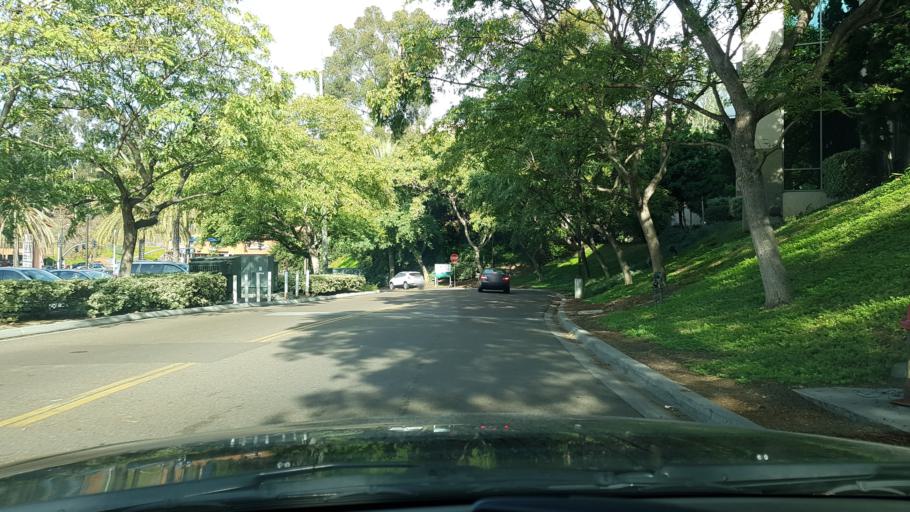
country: US
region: California
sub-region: San Diego County
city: Poway
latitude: 32.9158
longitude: -117.1137
